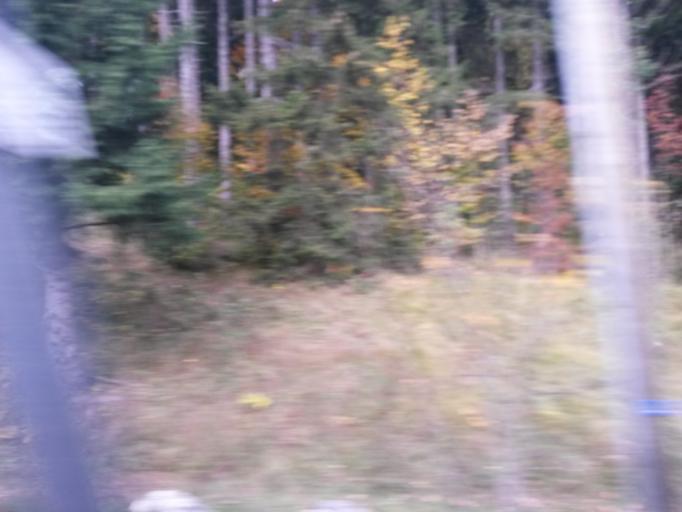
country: CH
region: Vaud
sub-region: Nyon District
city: Saint-Cergue
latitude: 46.4517
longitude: 6.1264
